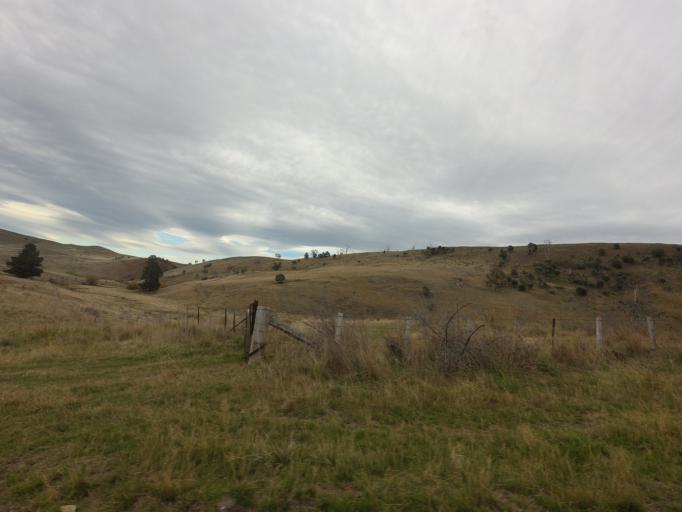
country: AU
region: Tasmania
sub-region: Derwent Valley
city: New Norfolk
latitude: -42.3628
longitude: 146.8427
